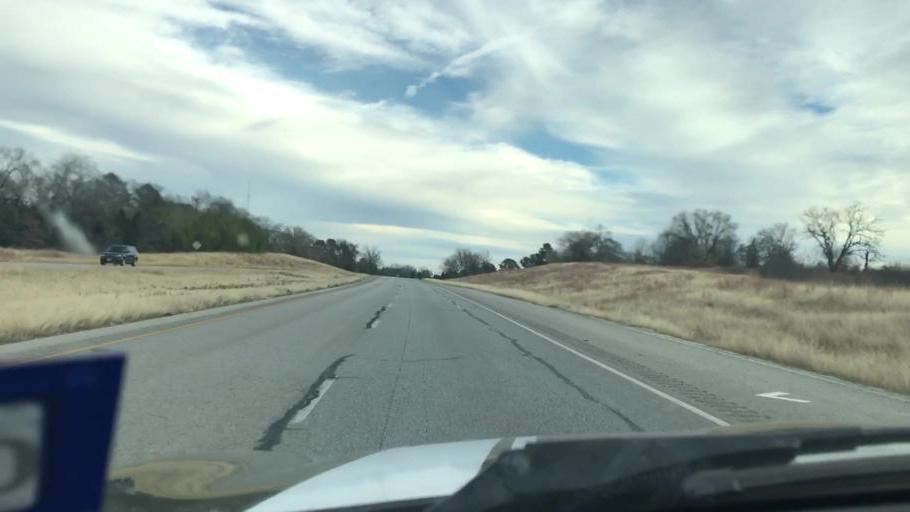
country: US
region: Texas
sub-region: Bastrop County
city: Elgin
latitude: 30.3032
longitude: -97.2949
